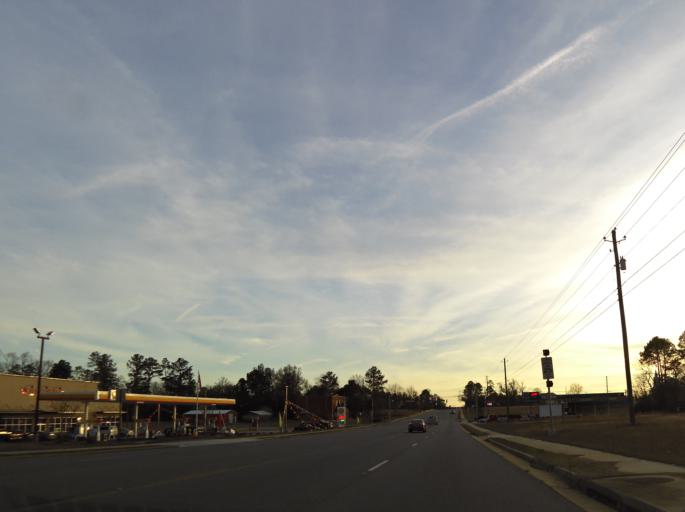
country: US
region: Georgia
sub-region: Houston County
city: Centerville
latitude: 32.7262
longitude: -83.6840
